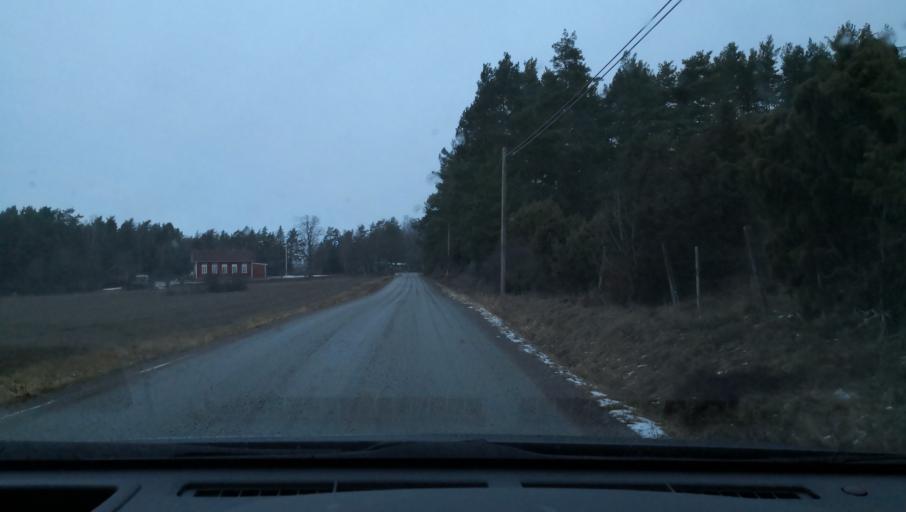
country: SE
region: Uppsala
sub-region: Enkopings Kommun
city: Hummelsta
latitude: 59.4552
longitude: 16.8551
